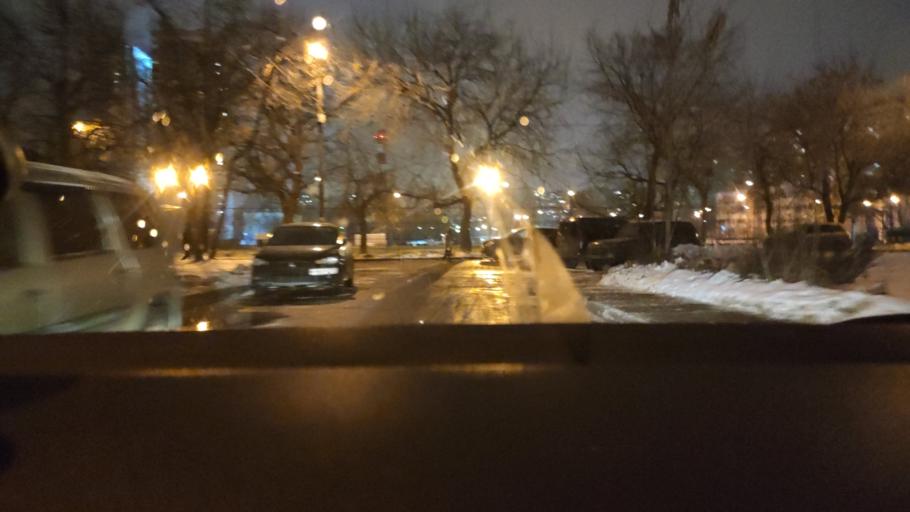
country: RU
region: Moscow
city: Solntsevo
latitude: 55.6414
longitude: 37.4049
